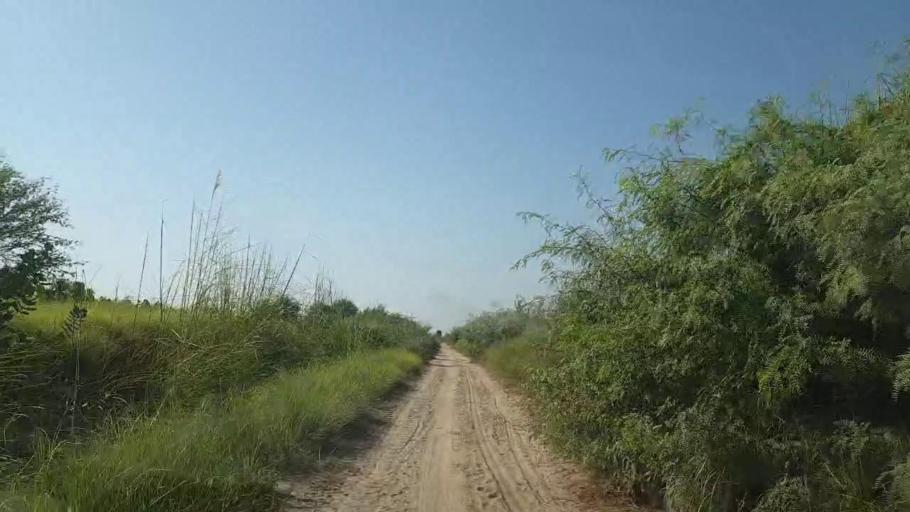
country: PK
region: Sindh
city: Tando Jam
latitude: 25.3188
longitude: 68.6021
